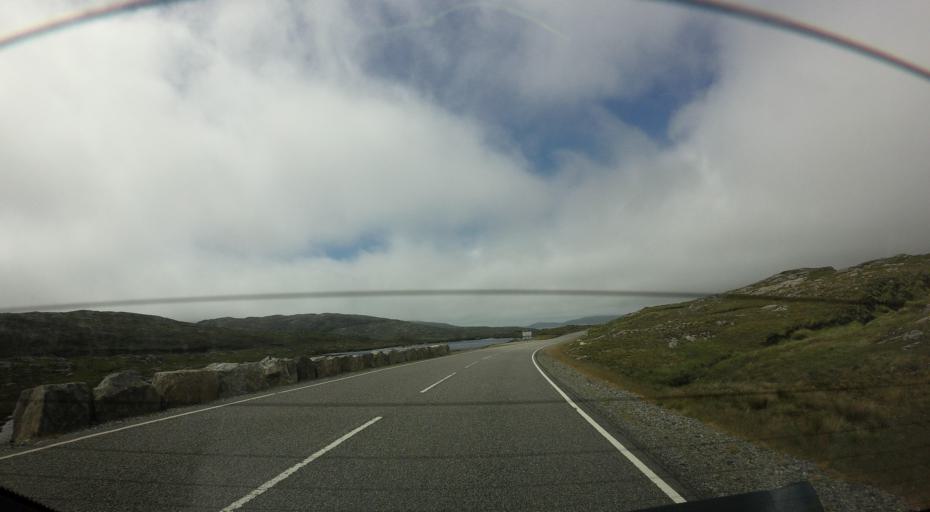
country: GB
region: Scotland
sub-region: Eilean Siar
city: Harris
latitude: 57.8567
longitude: -6.8550
